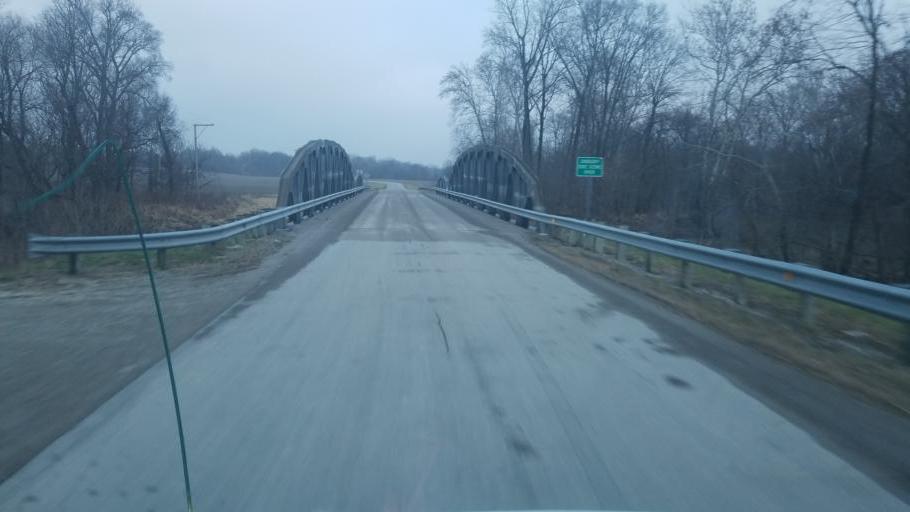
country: US
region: Ohio
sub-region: Seneca County
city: Tiffin
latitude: 40.9890
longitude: -83.2043
